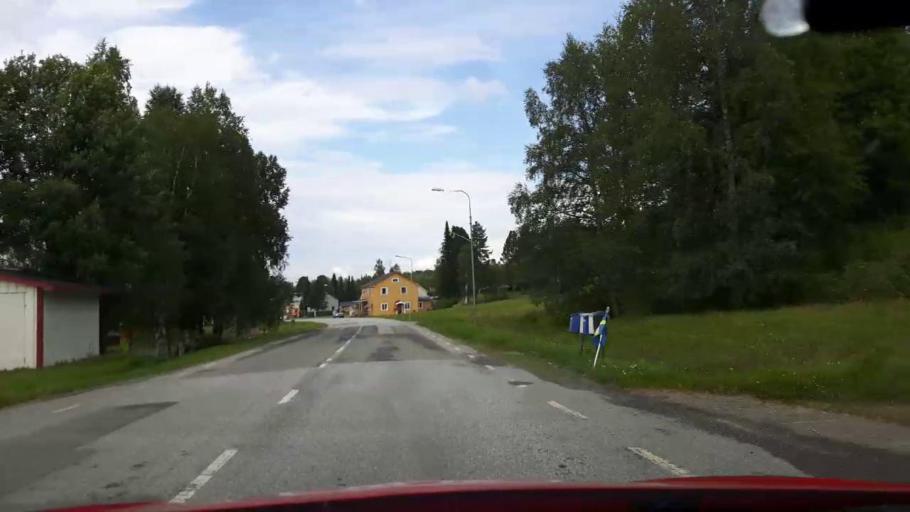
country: SE
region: Jaemtland
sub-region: Stroemsunds Kommun
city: Stroemsund
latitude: 64.4330
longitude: 15.5953
